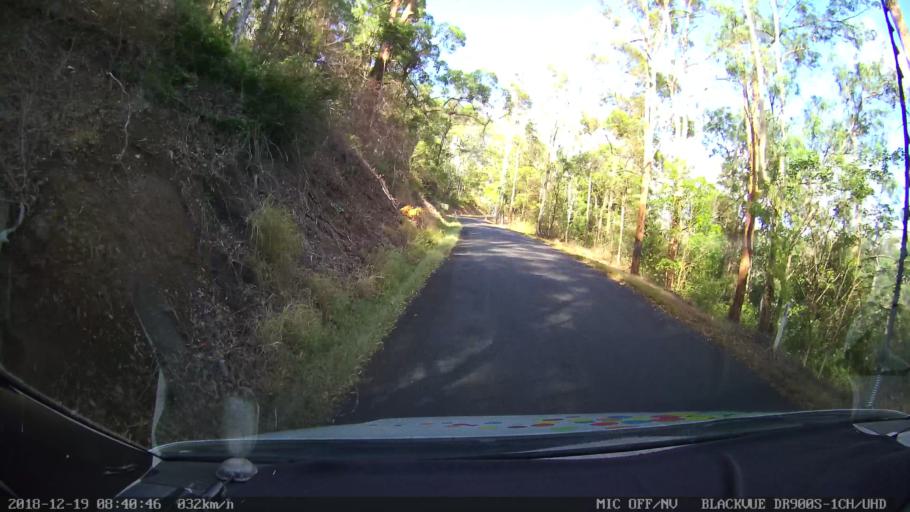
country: AU
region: New South Wales
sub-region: Kyogle
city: Kyogle
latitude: -28.3414
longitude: 152.9684
